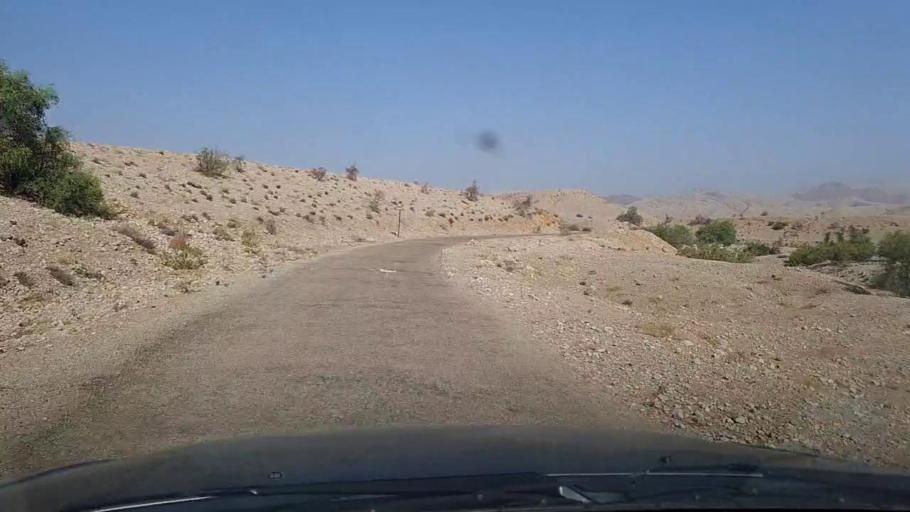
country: PK
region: Sindh
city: Sann
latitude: 25.8803
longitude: 67.9538
